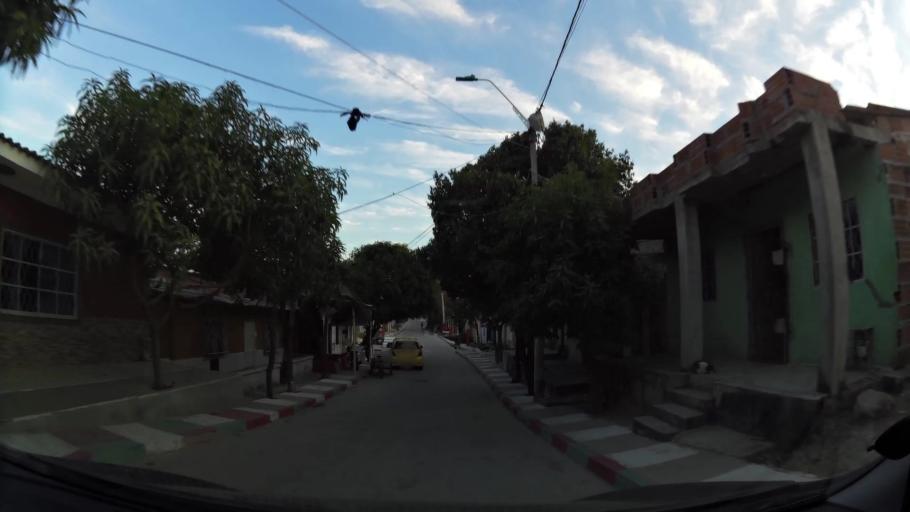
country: CO
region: Atlantico
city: Barranquilla
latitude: 10.9631
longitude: -74.8274
